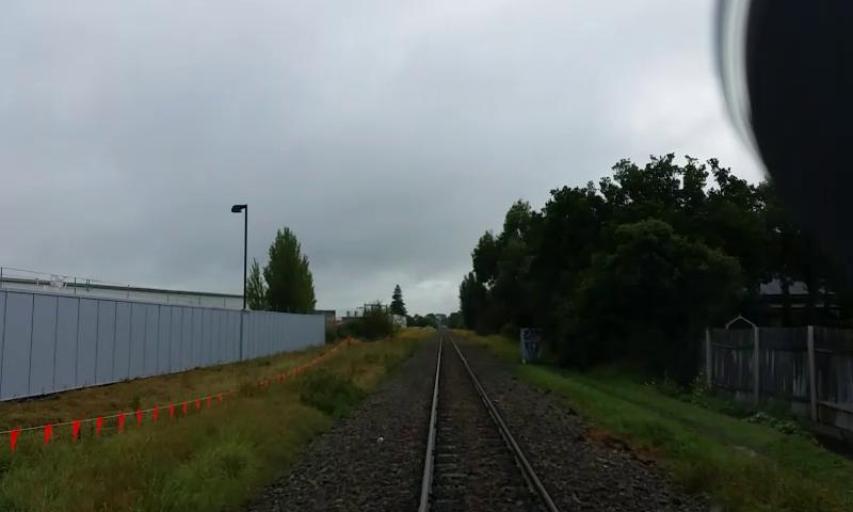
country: NZ
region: Canterbury
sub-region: Christchurch City
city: Christchurch
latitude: -43.5341
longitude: 172.6094
